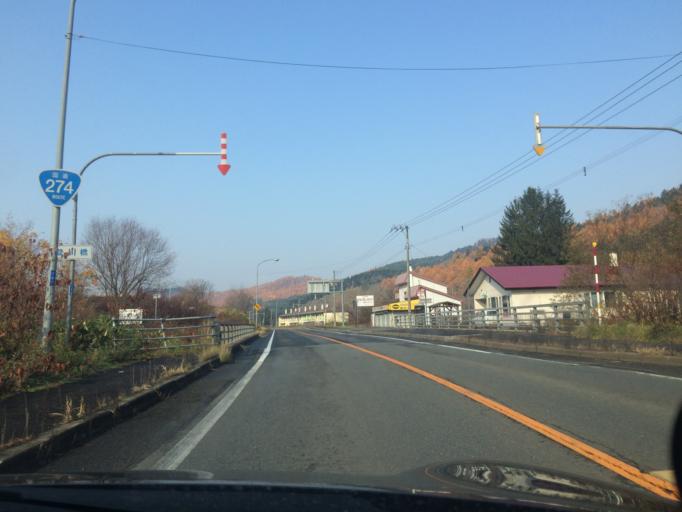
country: JP
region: Hokkaido
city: Iwamizawa
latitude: 42.9314
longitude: 142.0939
